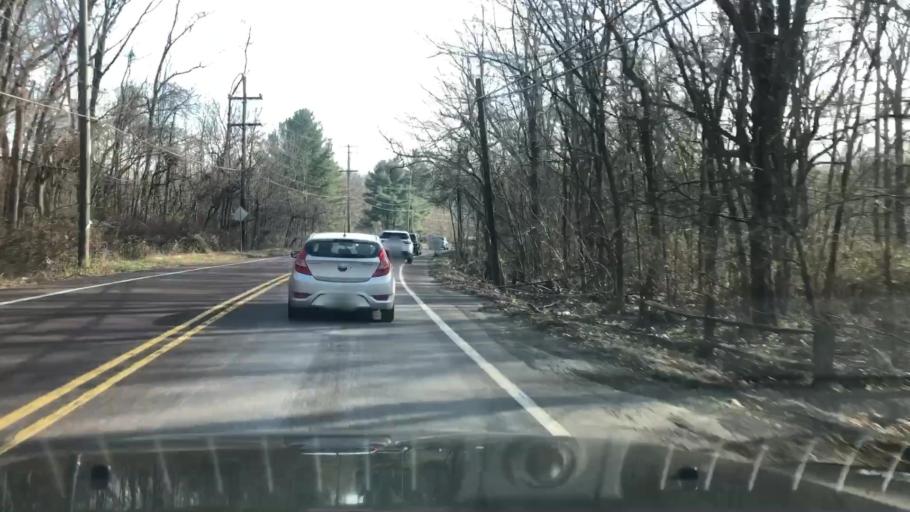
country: US
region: Pennsylvania
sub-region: Bucks County
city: Langhorne
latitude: 40.1892
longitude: -74.9246
